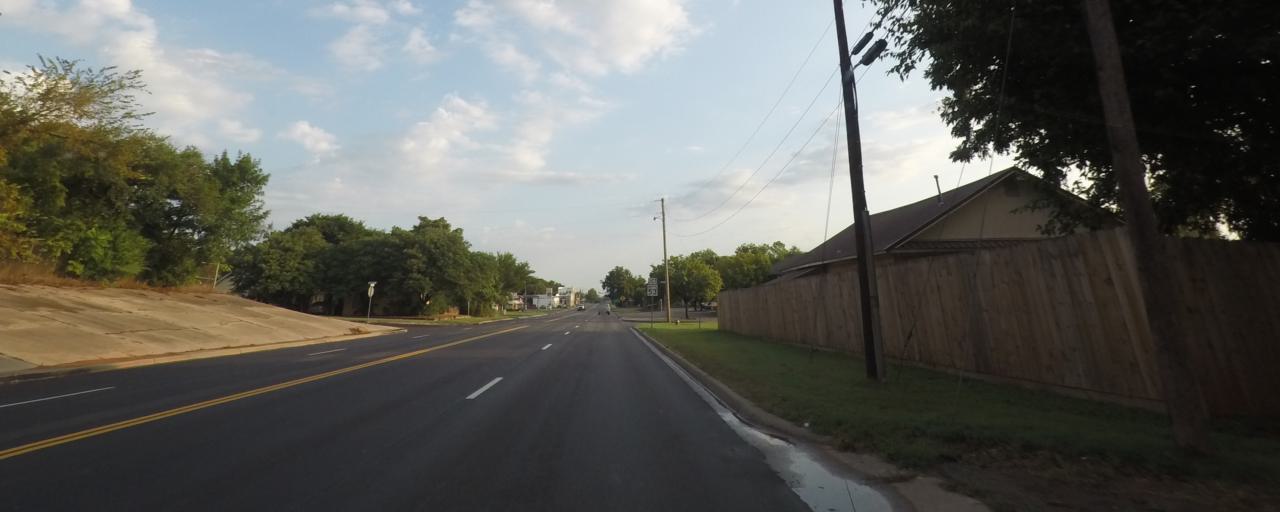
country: US
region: Oklahoma
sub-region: Stephens County
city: Comanche
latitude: 34.3652
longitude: -97.9642
